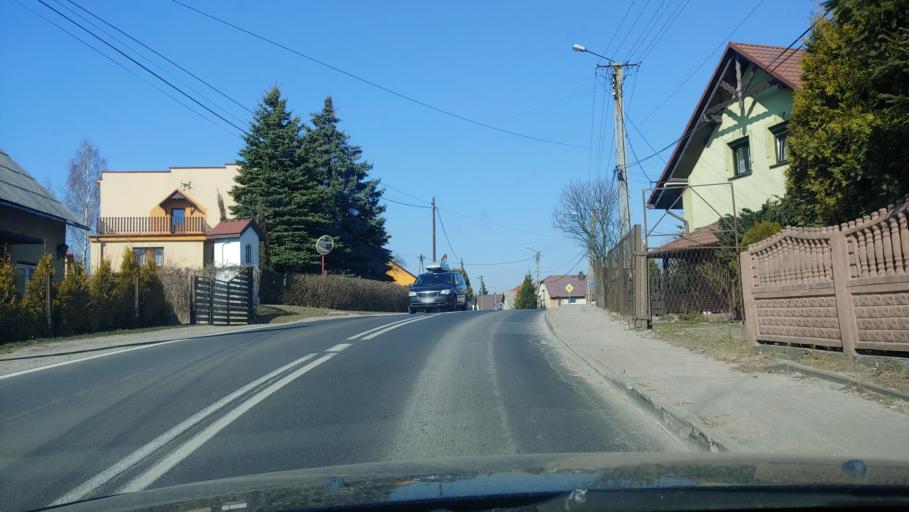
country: PL
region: Lesser Poland Voivodeship
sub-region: Powiat chrzanowski
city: Myslachowice
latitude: 50.1813
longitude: 19.4757
